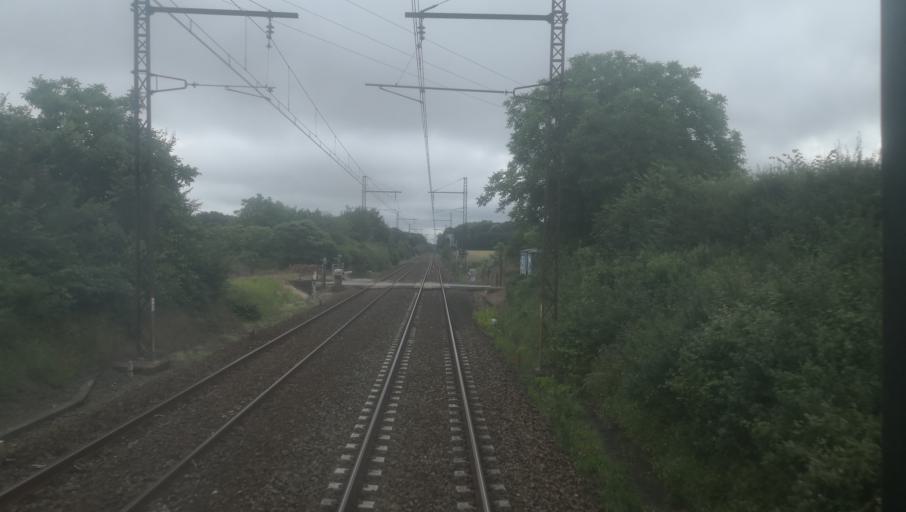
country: FR
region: Centre
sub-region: Departement de l'Indre
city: Montierchaume
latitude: 46.8310
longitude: 1.7504
